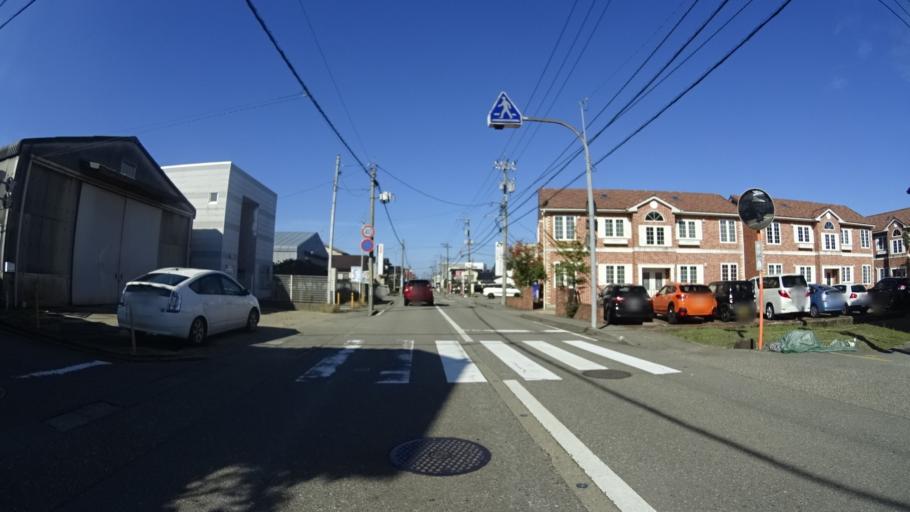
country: JP
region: Ishikawa
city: Kanazawa-shi
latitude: 36.5942
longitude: 136.6100
